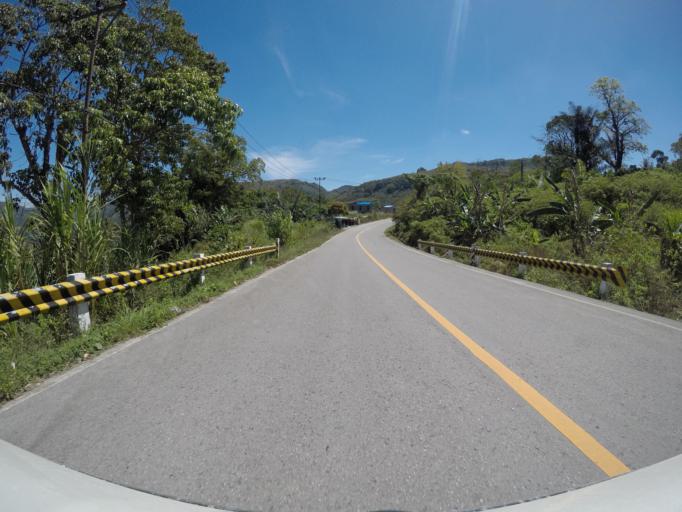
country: TL
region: Manatuto
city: Manatuto
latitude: -8.7808
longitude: 125.9674
